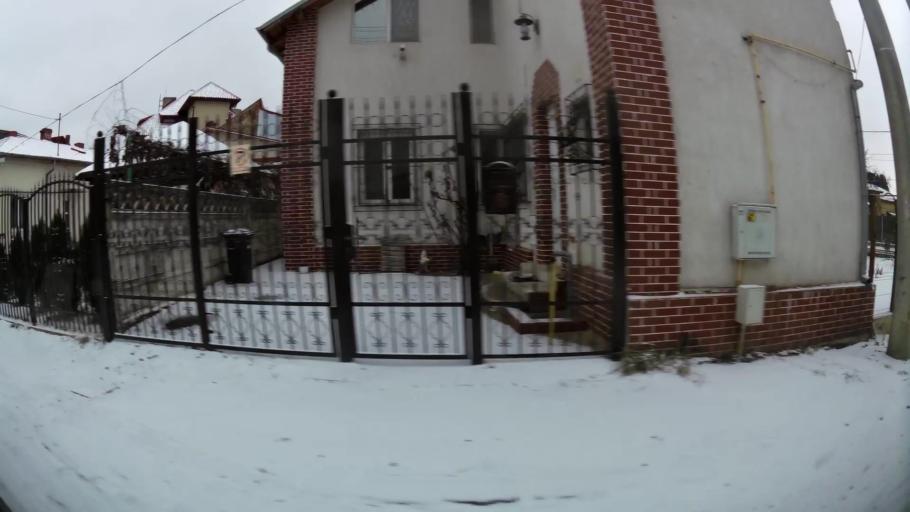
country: RO
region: Prahova
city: Ploiesti
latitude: 44.9379
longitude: 26.0338
